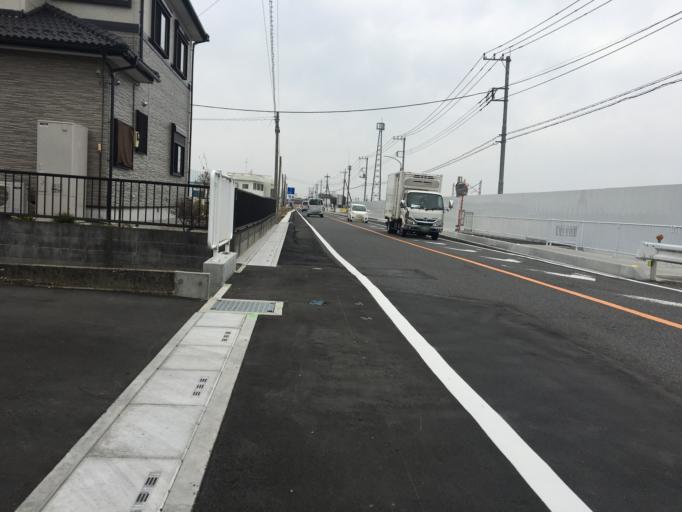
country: JP
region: Saitama
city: Kazo
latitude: 36.1180
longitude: 139.5965
